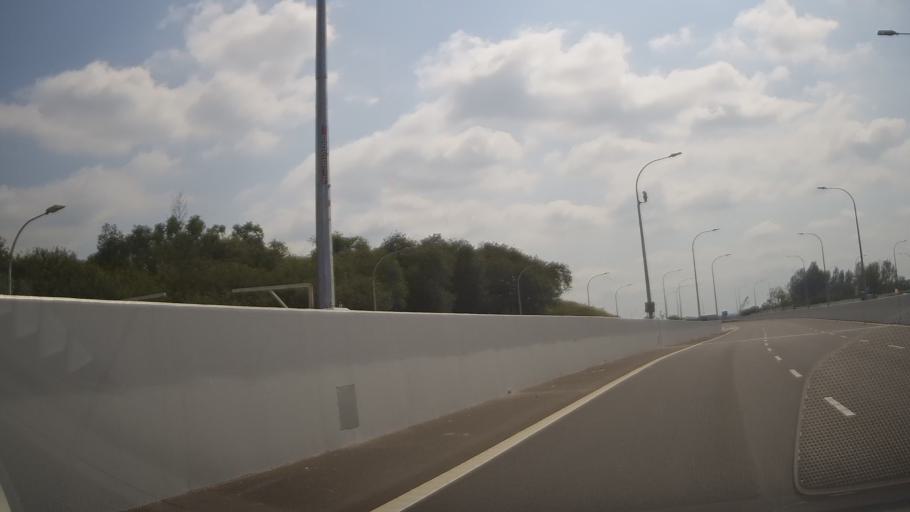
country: MY
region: Johor
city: Kampung Pasir Gudang Baru
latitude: 1.3853
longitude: 103.9183
